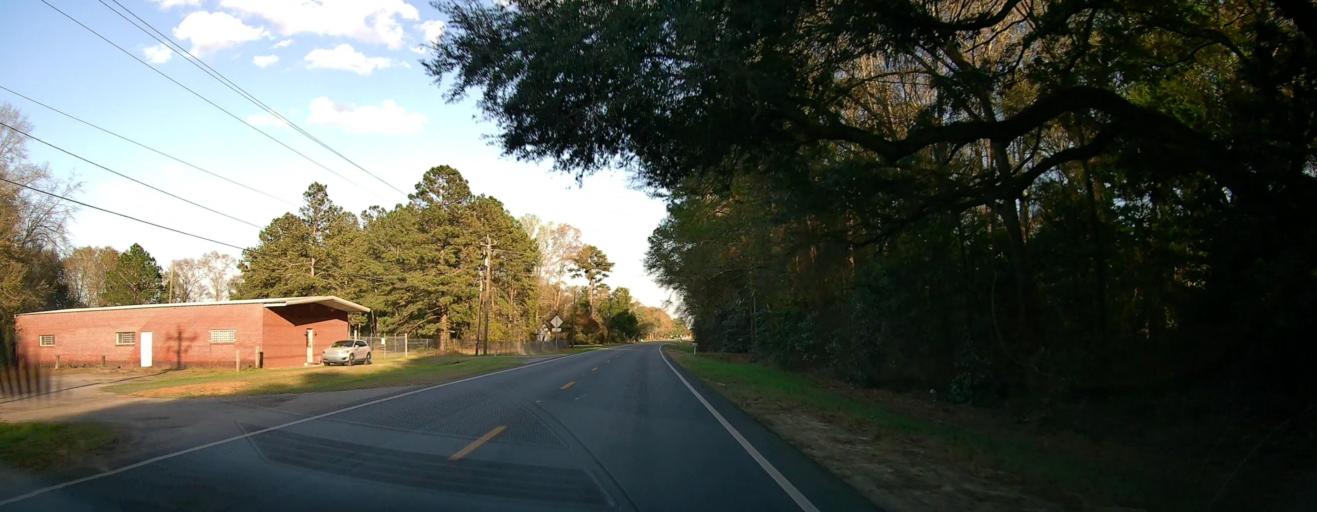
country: US
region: Georgia
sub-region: Evans County
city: Claxton
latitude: 32.1618
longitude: -81.8803
